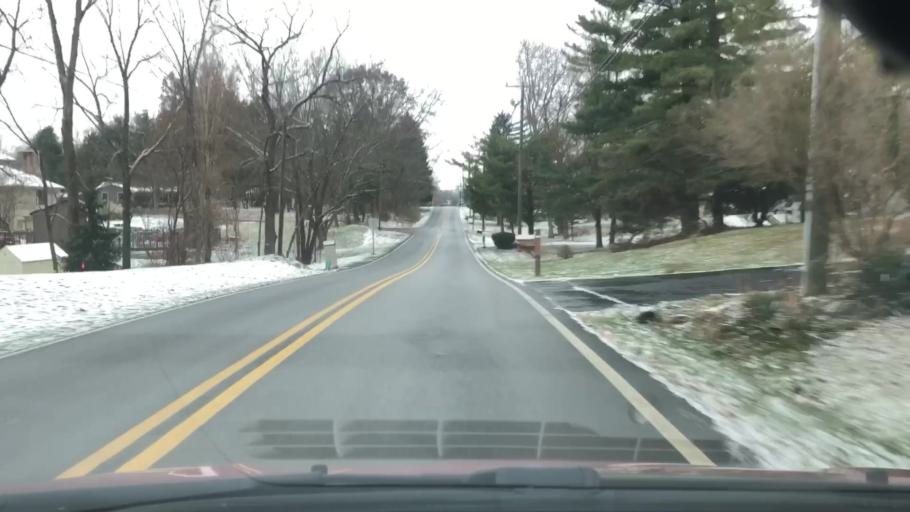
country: US
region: Ohio
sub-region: Franklin County
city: Westerville
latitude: 40.1714
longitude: -82.9272
